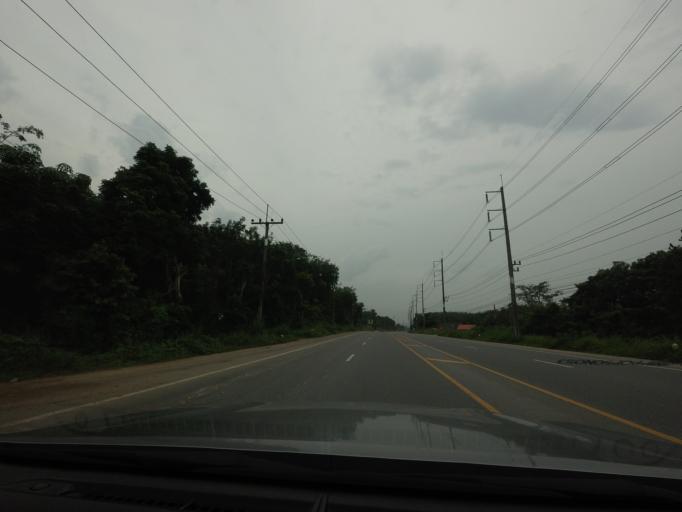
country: TH
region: Songkhla
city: Na Mom
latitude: 7.0524
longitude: 100.6501
